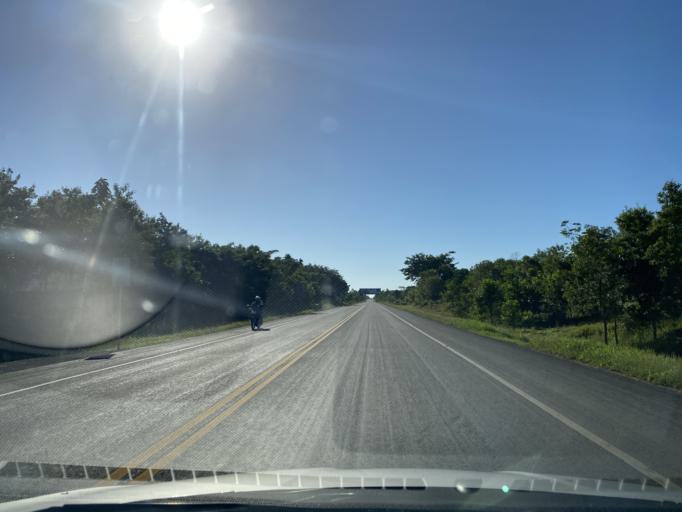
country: DO
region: Santo Domingo
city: Guerra
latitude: 18.5235
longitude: -69.7477
